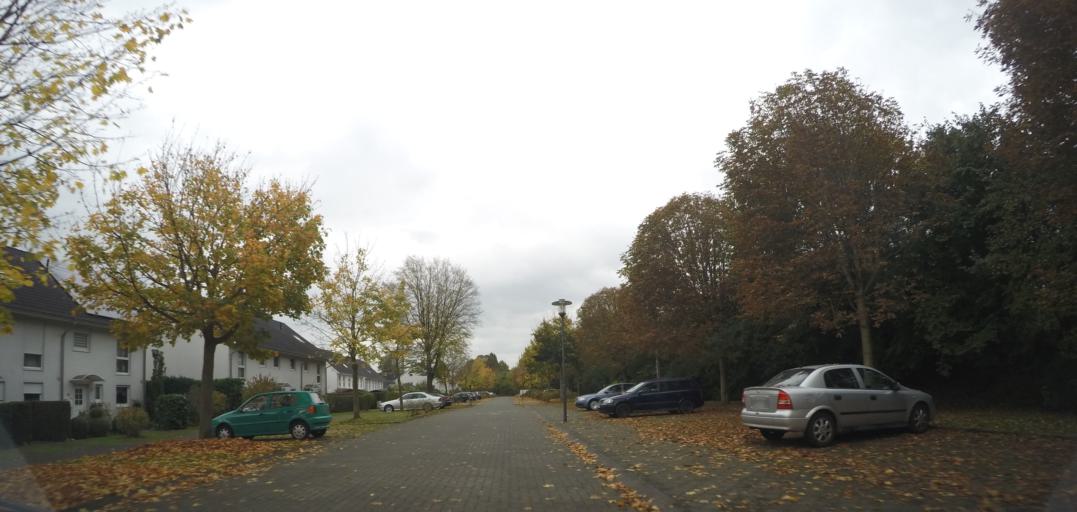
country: DE
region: North Rhine-Westphalia
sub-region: Regierungsbezirk Arnsberg
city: Lippstadt
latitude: 51.6605
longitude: 8.3465
